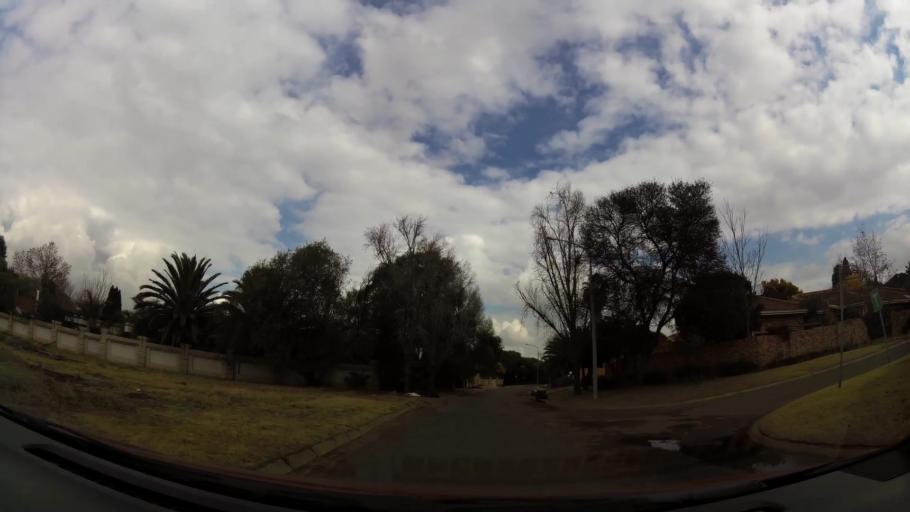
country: ZA
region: Gauteng
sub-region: Sedibeng District Municipality
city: Vanderbijlpark
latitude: -26.7399
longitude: 27.8509
